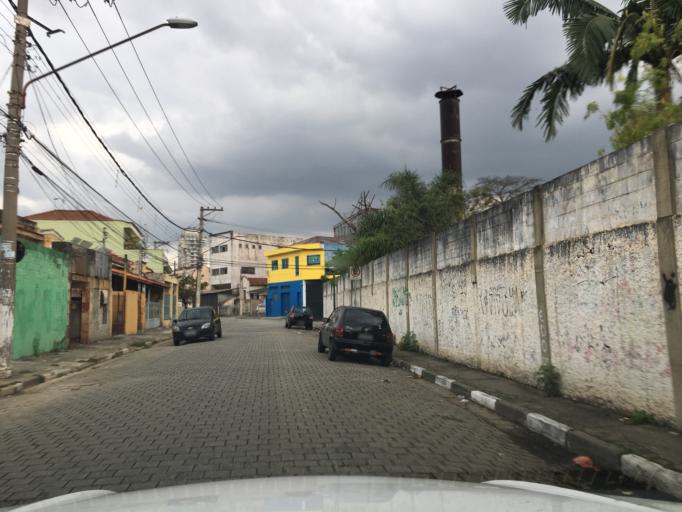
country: BR
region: Sao Paulo
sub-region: Guarulhos
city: Guarulhos
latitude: -23.4956
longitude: -46.5529
